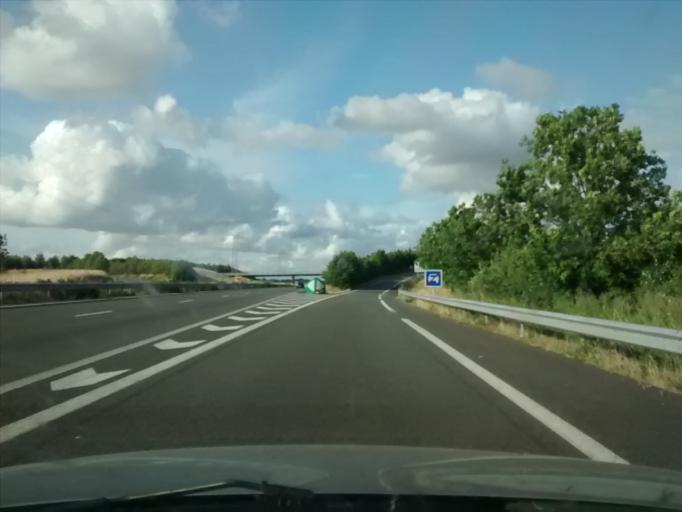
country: FR
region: Pays de la Loire
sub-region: Departement de la Mayenne
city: Louverne
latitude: 48.1278
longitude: -0.7184
